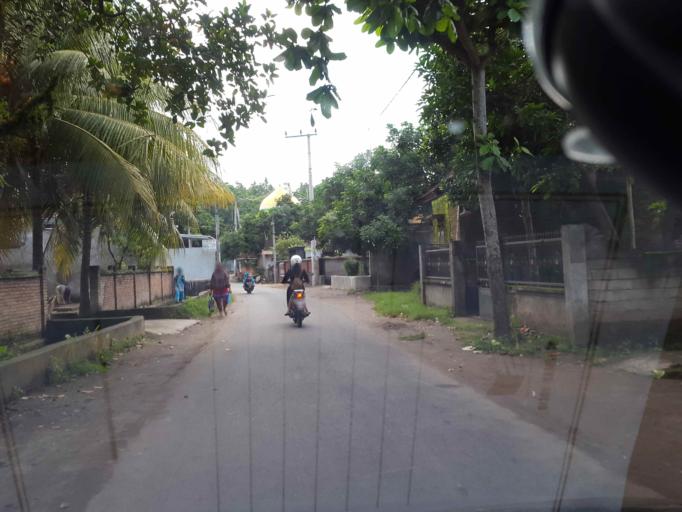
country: ID
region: West Nusa Tenggara
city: Mambalan
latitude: -8.5300
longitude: 116.0805
